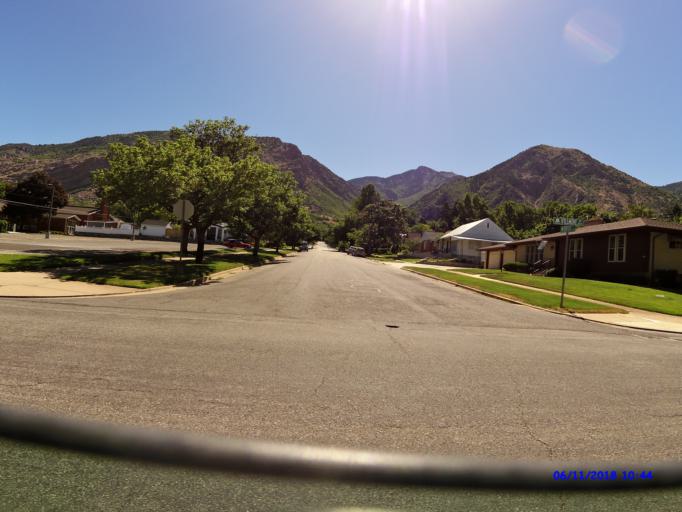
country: US
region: Utah
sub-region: Weber County
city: Ogden
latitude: 41.2172
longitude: -111.9373
